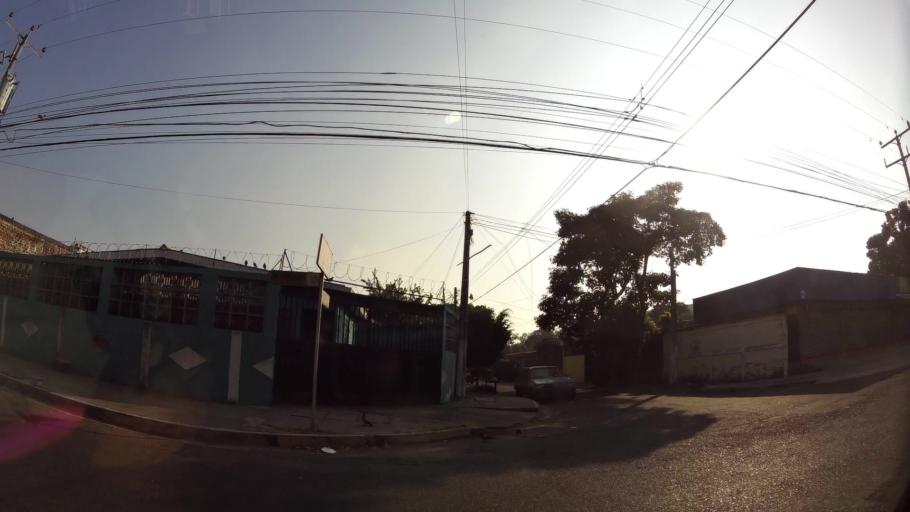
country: SV
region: La Libertad
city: Antiguo Cuscatlan
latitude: 13.6826
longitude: -89.2248
